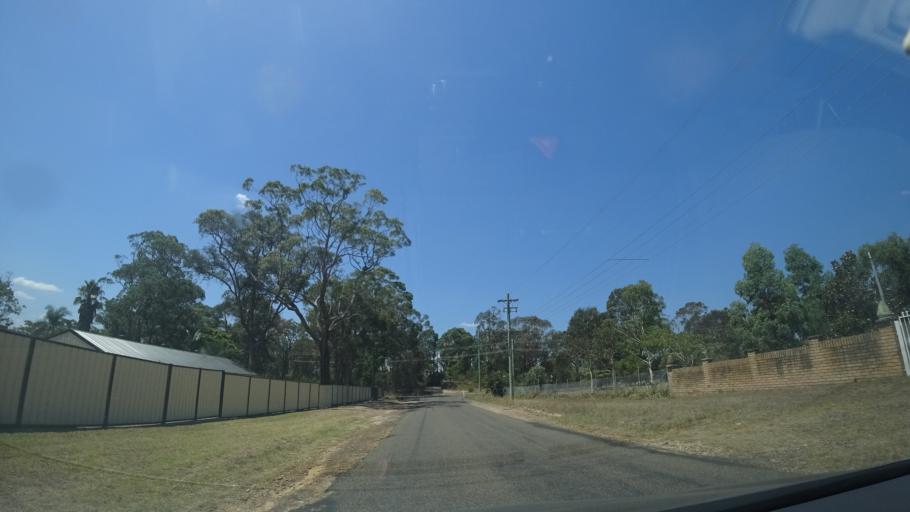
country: AU
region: New South Wales
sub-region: Wollondilly
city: Buxton
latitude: -34.2620
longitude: 150.5273
